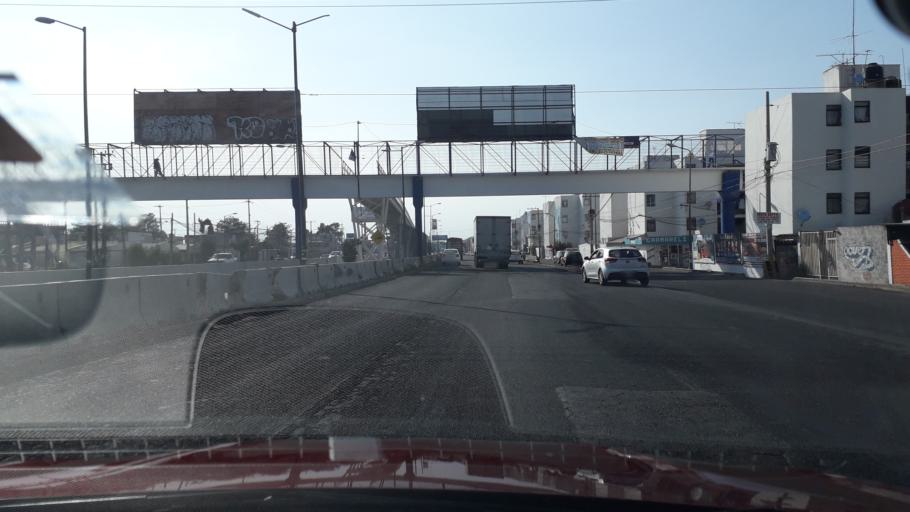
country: MX
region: Puebla
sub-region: Puebla
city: El Capulo (La Quebradora)
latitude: 18.9862
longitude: -98.2344
